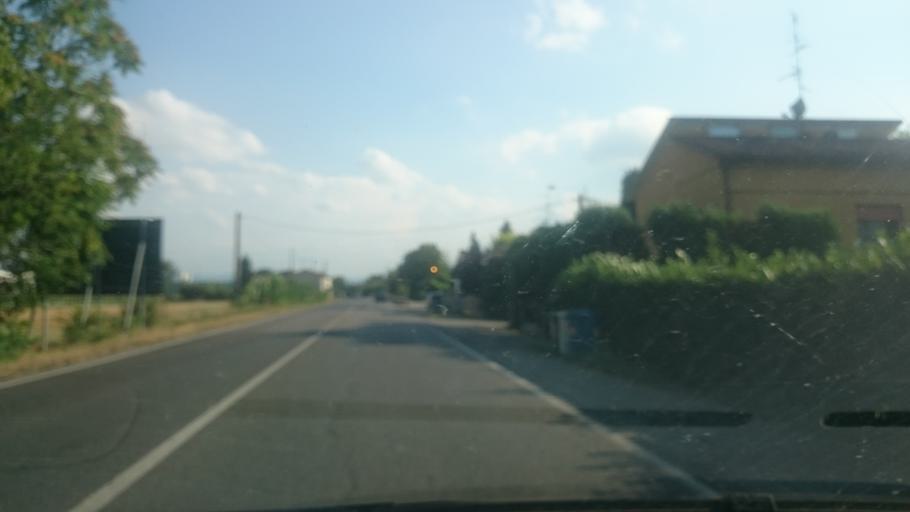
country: IT
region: Emilia-Romagna
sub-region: Provincia di Reggio Emilia
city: Rubiera
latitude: 44.6375
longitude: 10.7788
